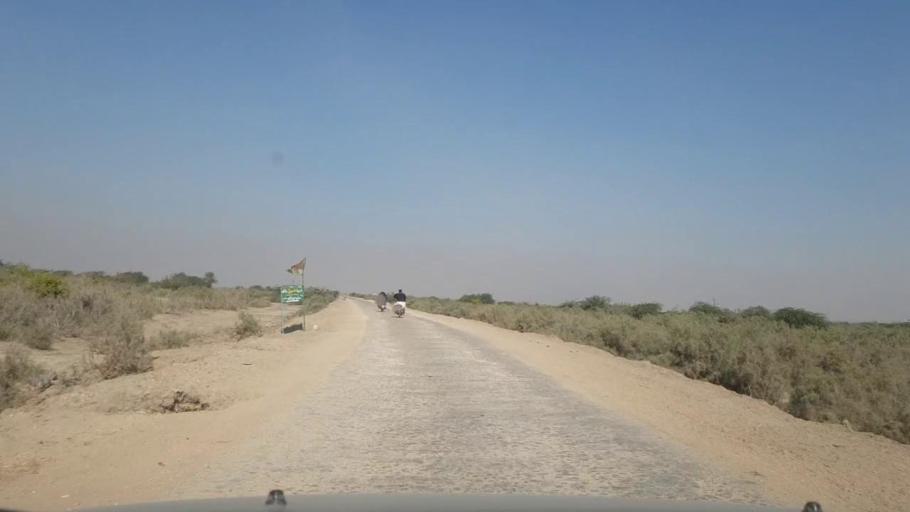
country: PK
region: Sindh
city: Thatta
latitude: 24.8075
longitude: 67.9008
